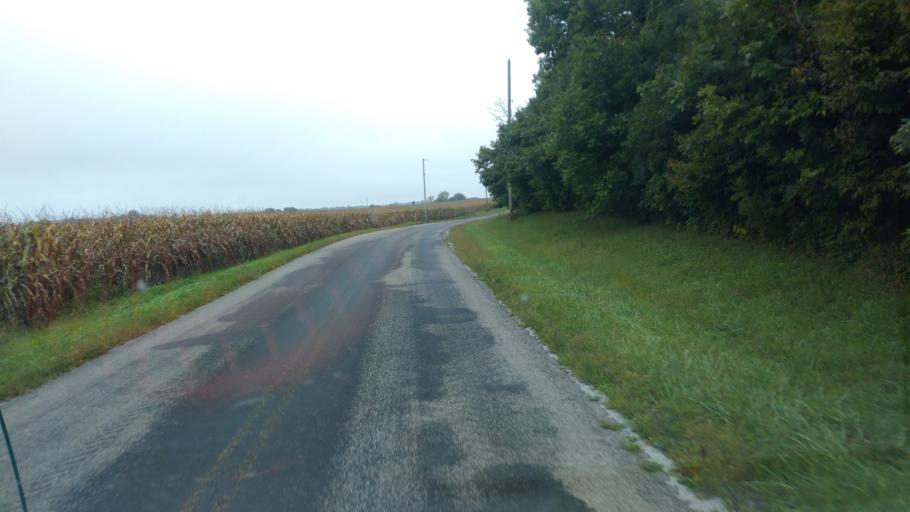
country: US
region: Ohio
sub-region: Logan County
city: Northwood
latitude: 40.5302
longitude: -83.6293
